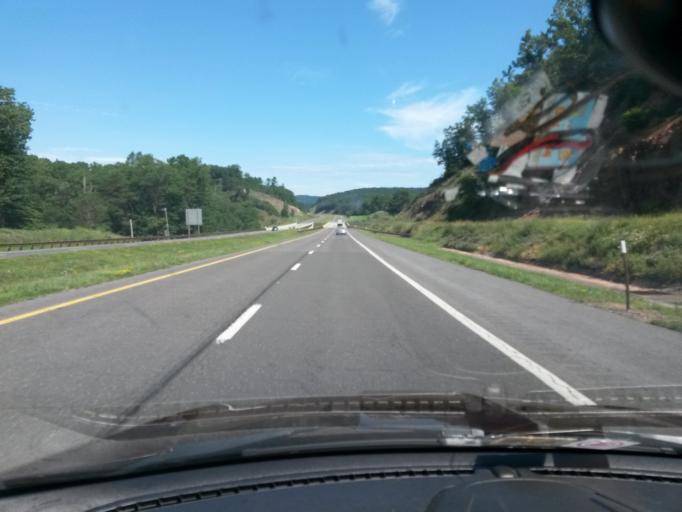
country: US
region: West Virginia
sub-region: Hardy County
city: Moorefield
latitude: 39.0536
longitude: -78.7793
